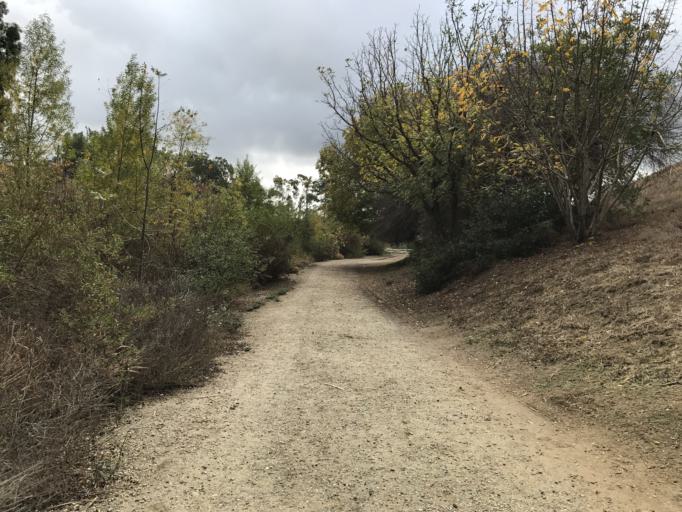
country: US
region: California
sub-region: Los Angeles County
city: Belvedere
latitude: 34.0715
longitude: -118.1892
